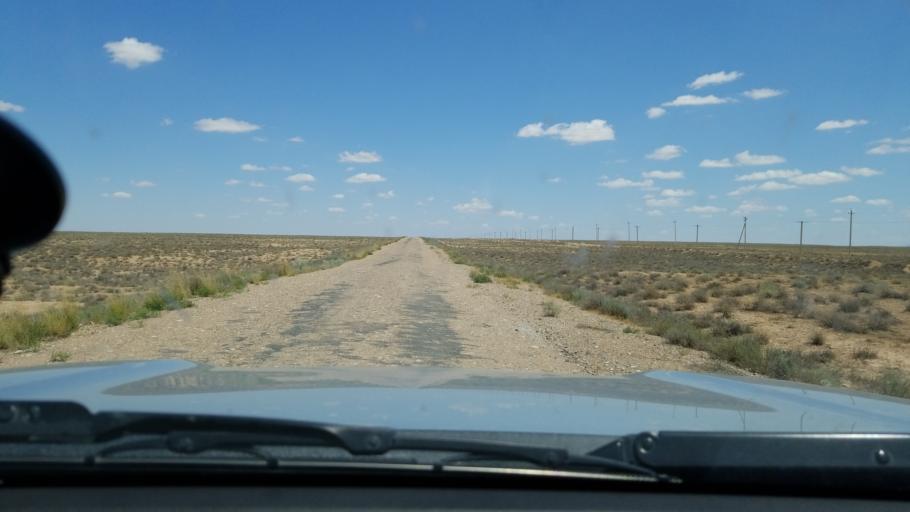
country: TM
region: Balkan
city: Turkmenbasy
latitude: 40.1526
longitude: 53.6847
